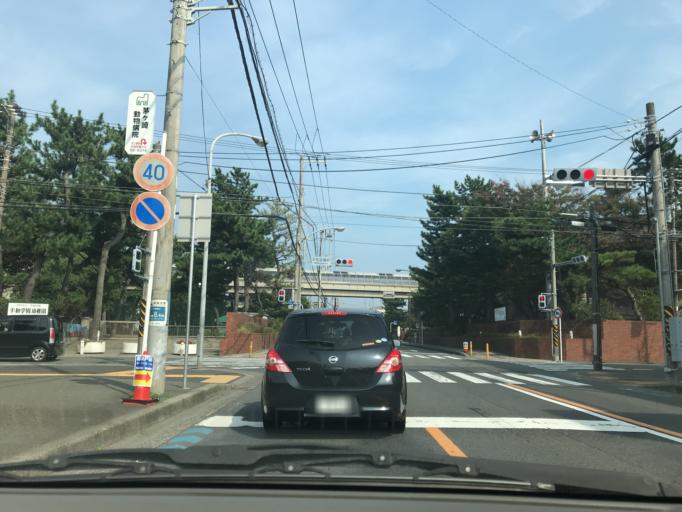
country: JP
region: Kanagawa
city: Chigasaki
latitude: 35.3256
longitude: 139.4311
